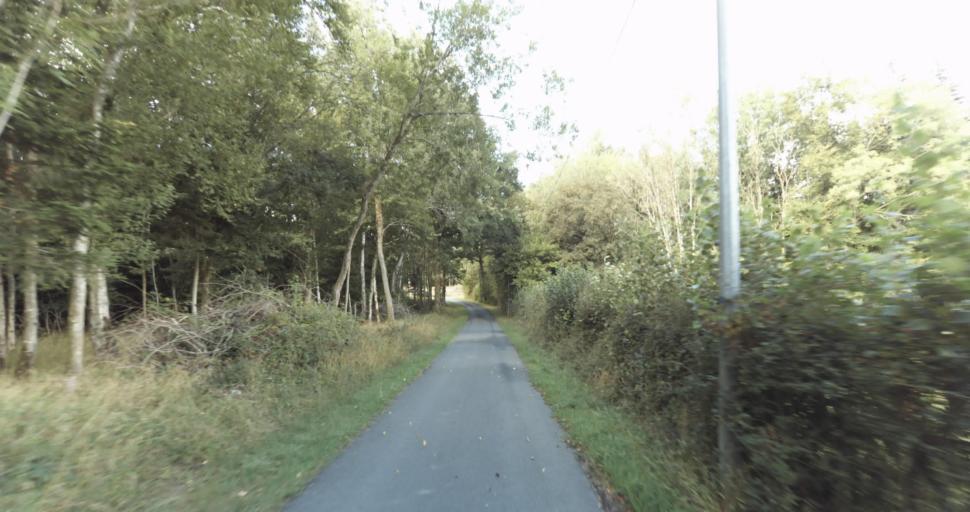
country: FR
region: Lower Normandy
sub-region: Departement de l'Orne
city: Gace
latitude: 48.7855
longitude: 0.3554
